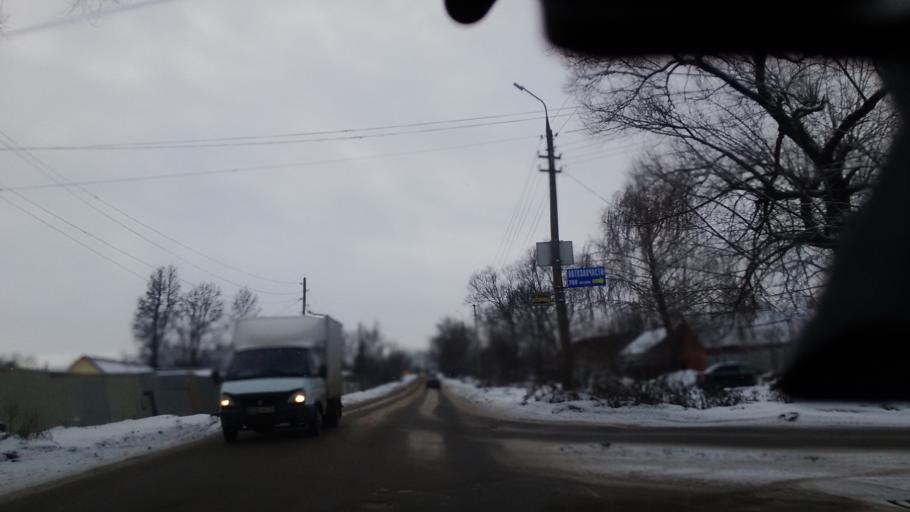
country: RU
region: Tula
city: Bogoroditsk
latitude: 53.7657
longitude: 38.1101
